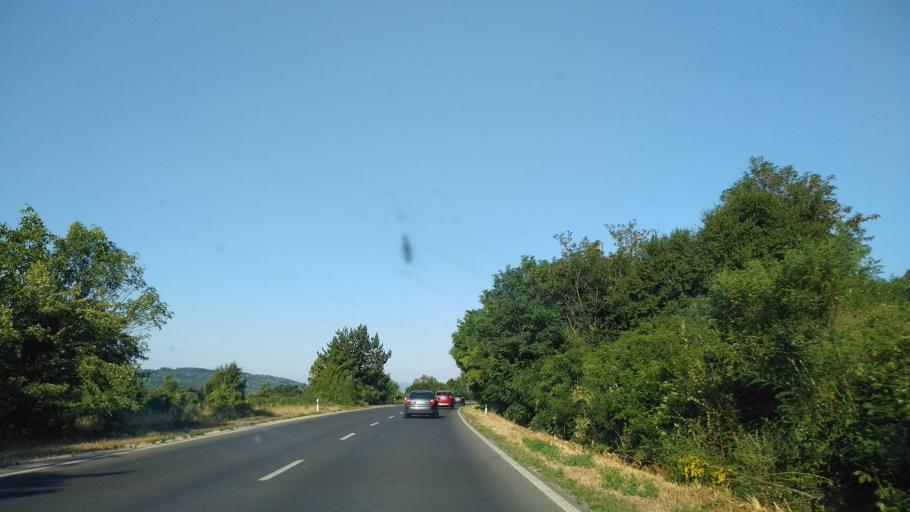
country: BG
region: Gabrovo
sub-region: Obshtina Sevlievo
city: Sevlievo
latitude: 43.0452
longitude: 25.2300
